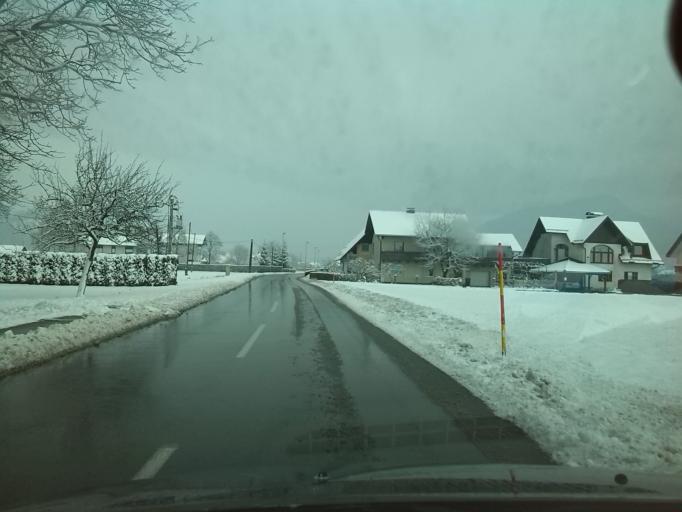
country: SI
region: Kamnik
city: Smarca
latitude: 46.2120
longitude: 14.5914
